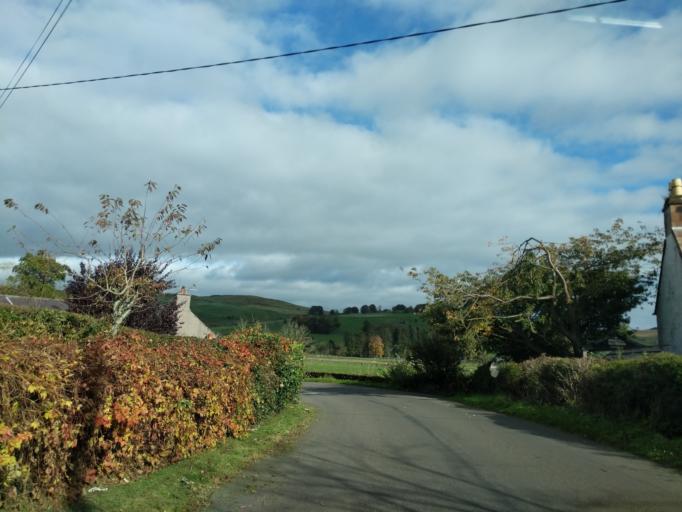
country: GB
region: Scotland
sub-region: Dumfries and Galloway
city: Thornhill
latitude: 55.1922
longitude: -3.9209
